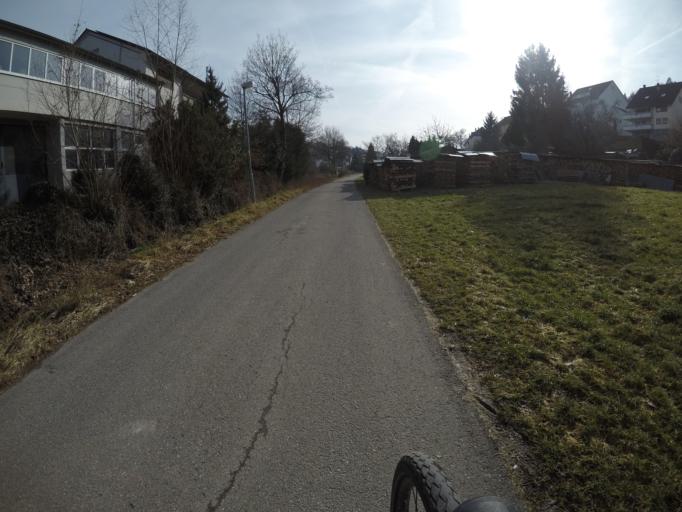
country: DE
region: Baden-Wuerttemberg
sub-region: Karlsruhe Region
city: Wildberg
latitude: 48.6194
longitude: 8.7776
